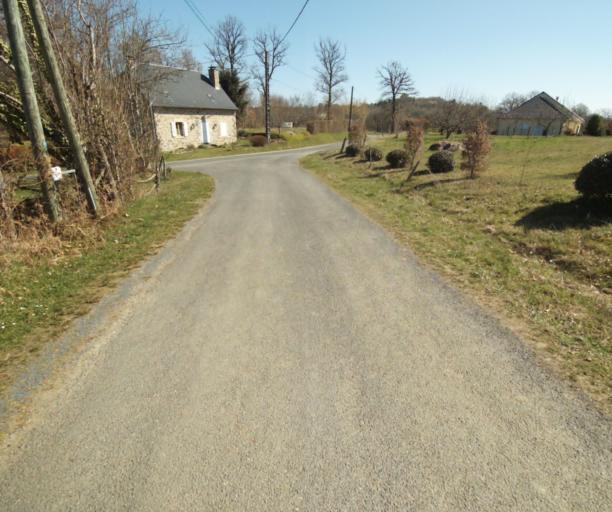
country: FR
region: Limousin
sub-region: Departement de la Correze
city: Saint-Clement
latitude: 45.3384
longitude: 1.6470
